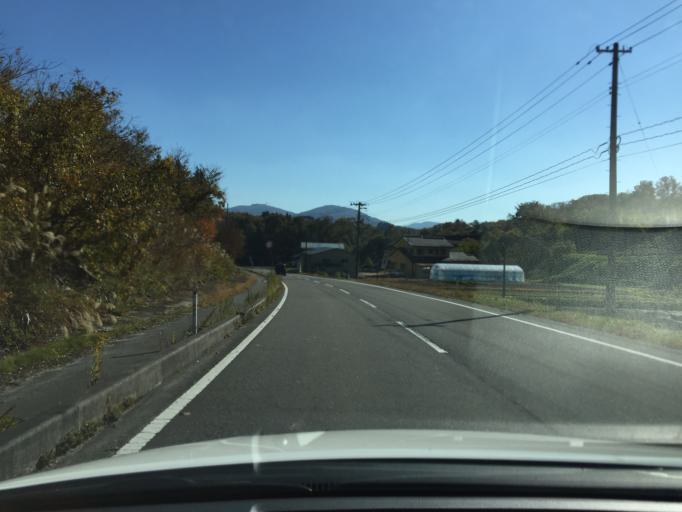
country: JP
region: Fukushima
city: Miharu
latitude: 37.4286
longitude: 140.5180
